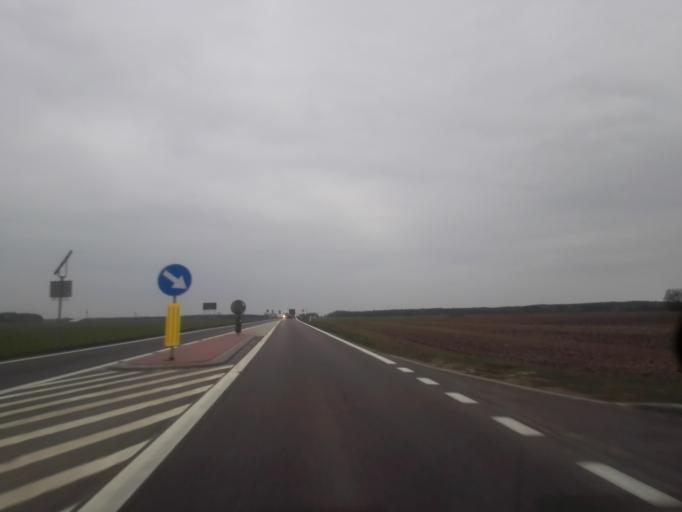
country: PL
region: Podlasie
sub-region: Powiat grajewski
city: Szczuczyn
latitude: 53.4991
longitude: 22.2312
